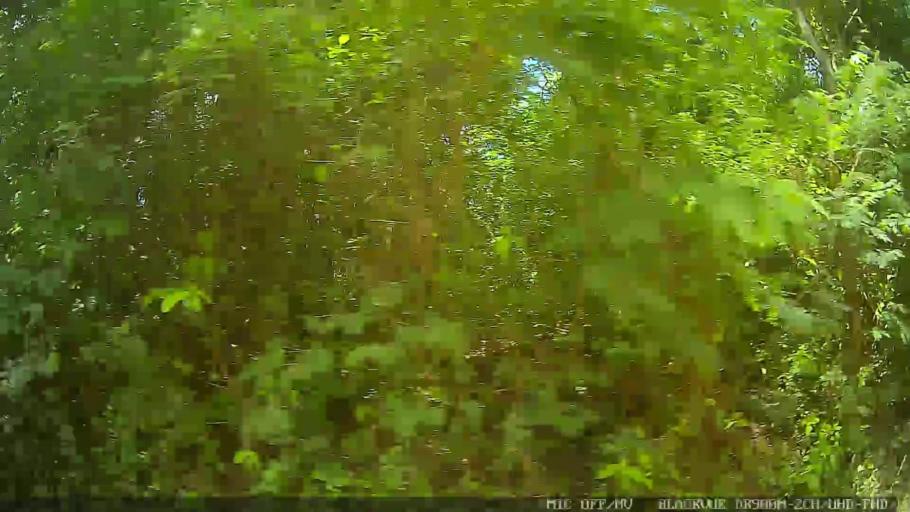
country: BR
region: Sao Paulo
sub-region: Conchas
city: Conchas
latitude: -23.0511
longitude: -47.9875
